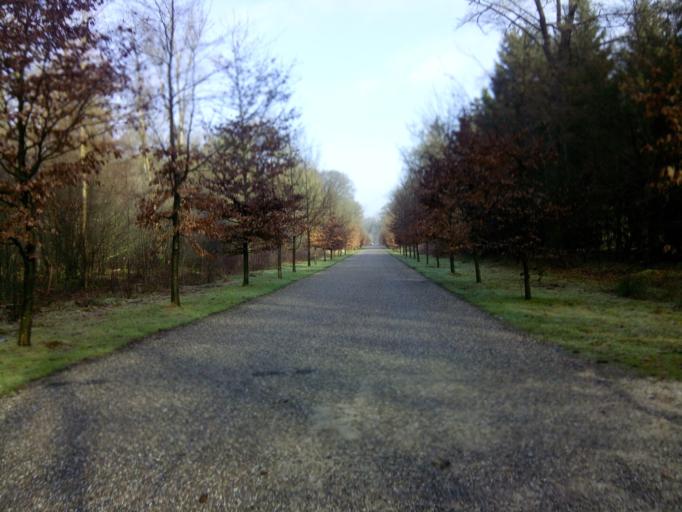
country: NL
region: Utrecht
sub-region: Gemeente Utrechtse Heuvelrug
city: Maarsbergen
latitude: 52.0436
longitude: 5.3982
